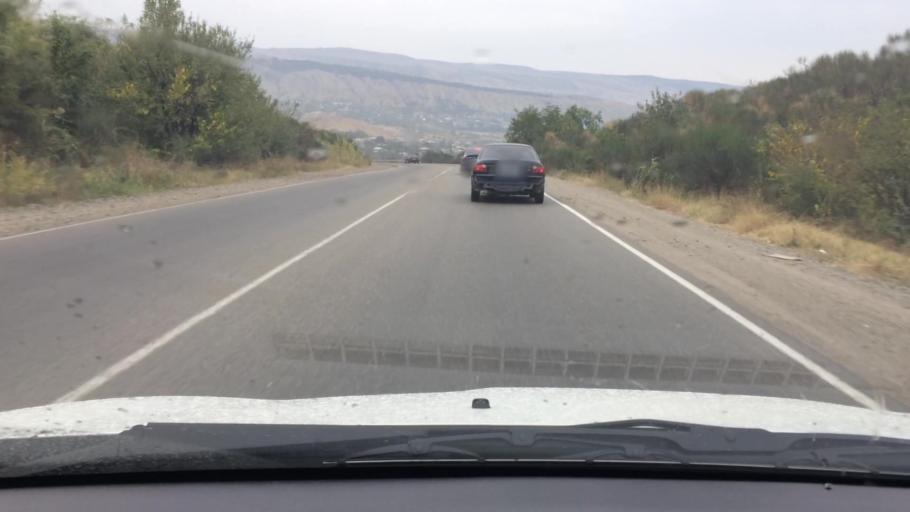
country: GE
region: T'bilisi
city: Tbilisi
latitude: 41.5928
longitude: 44.7805
